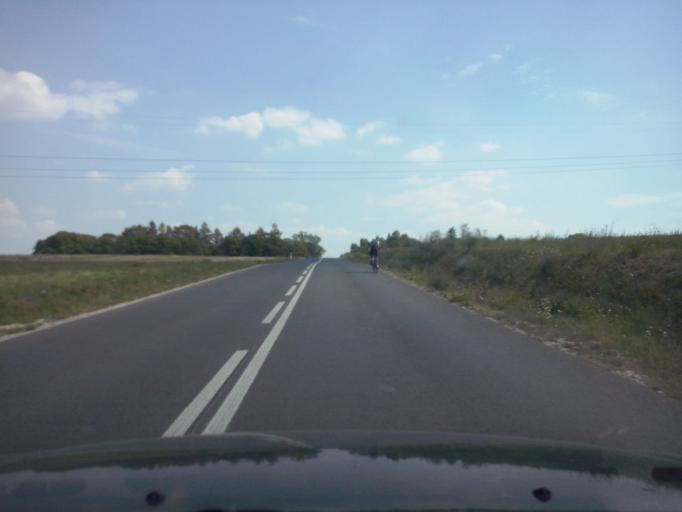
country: PL
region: Swietokrzyskie
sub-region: Powiat buski
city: Gnojno
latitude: 50.6062
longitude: 20.8282
